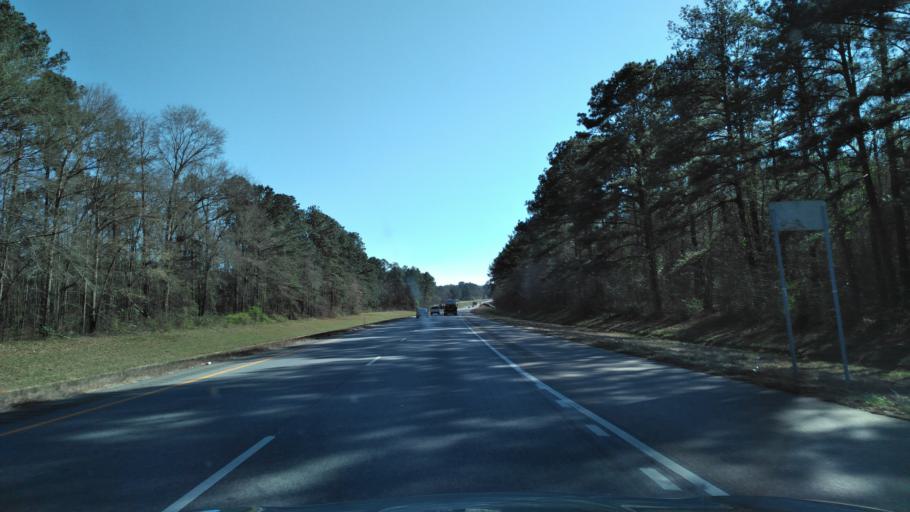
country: US
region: Alabama
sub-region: Butler County
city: Greenville
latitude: 31.8176
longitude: -86.6660
